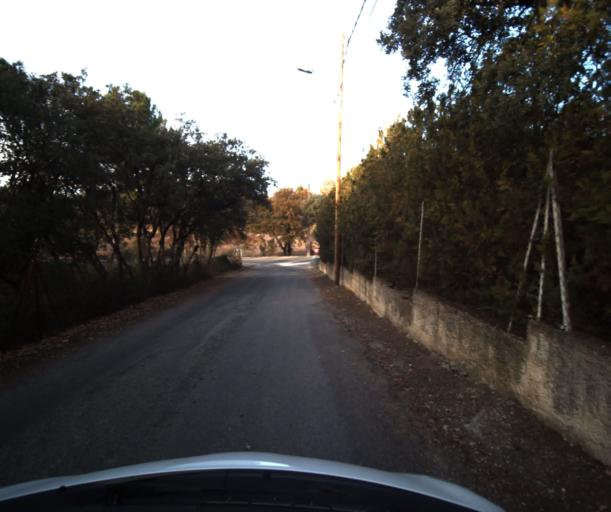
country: FR
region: Provence-Alpes-Cote d'Azur
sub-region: Departement du Vaucluse
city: Pertuis
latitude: 43.6955
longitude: 5.5333
